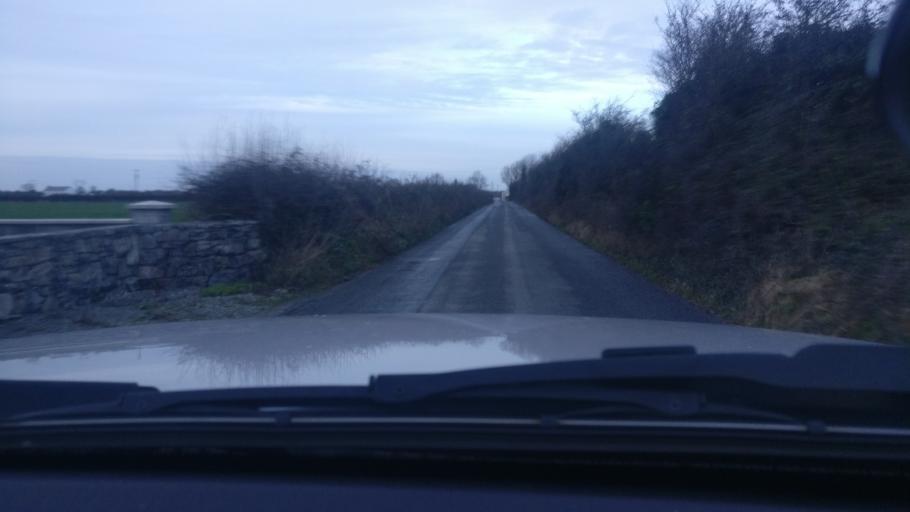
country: IE
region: Connaught
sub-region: County Galway
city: Loughrea
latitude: 53.1970
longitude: -8.5092
